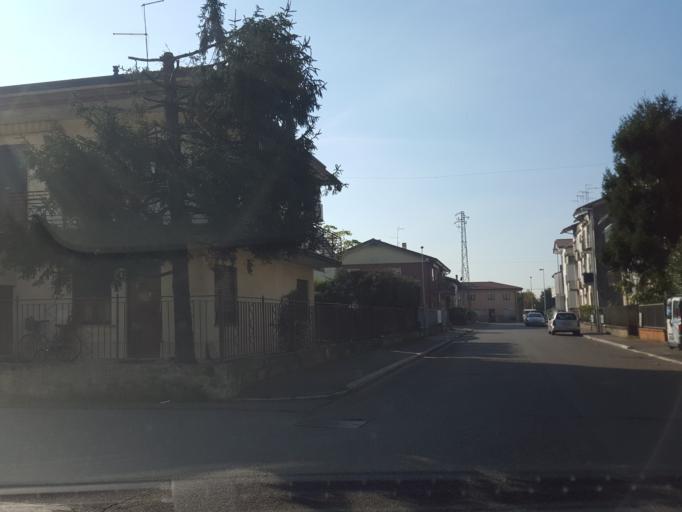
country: IT
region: Veneto
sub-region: Provincia di Verona
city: San Bonifacio
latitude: 45.3978
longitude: 11.2641
